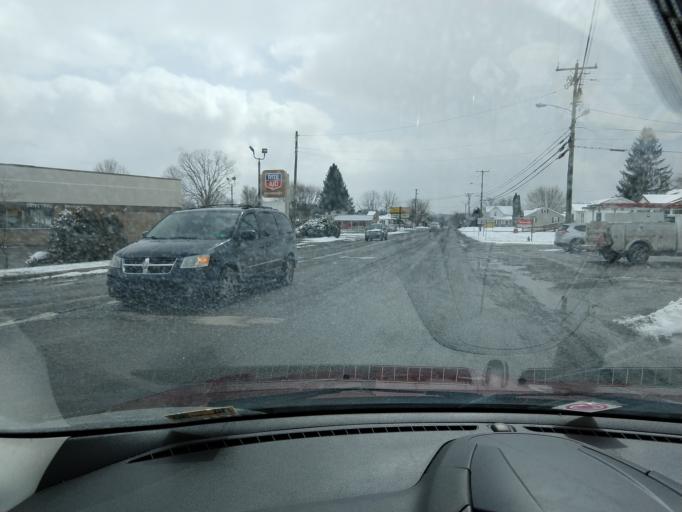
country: US
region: West Virginia
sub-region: Nicholas County
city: Craigsville
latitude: 38.3306
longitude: -80.6531
